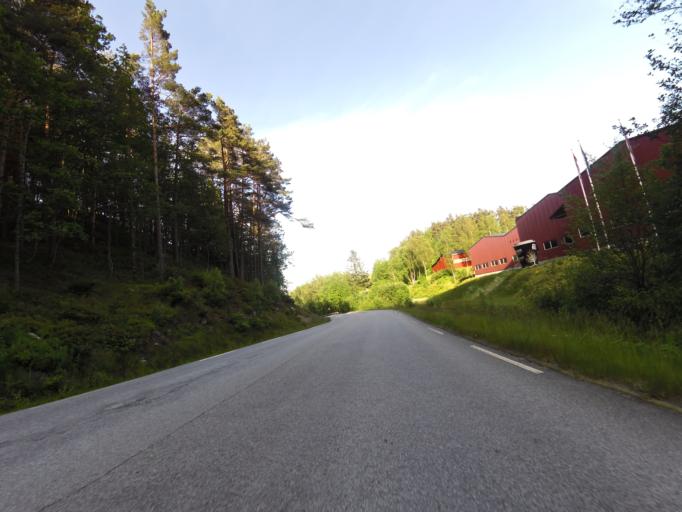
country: NO
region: Vest-Agder
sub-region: Flekkefjord
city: Flekkefjord
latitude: 58.2839
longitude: 6.6416
